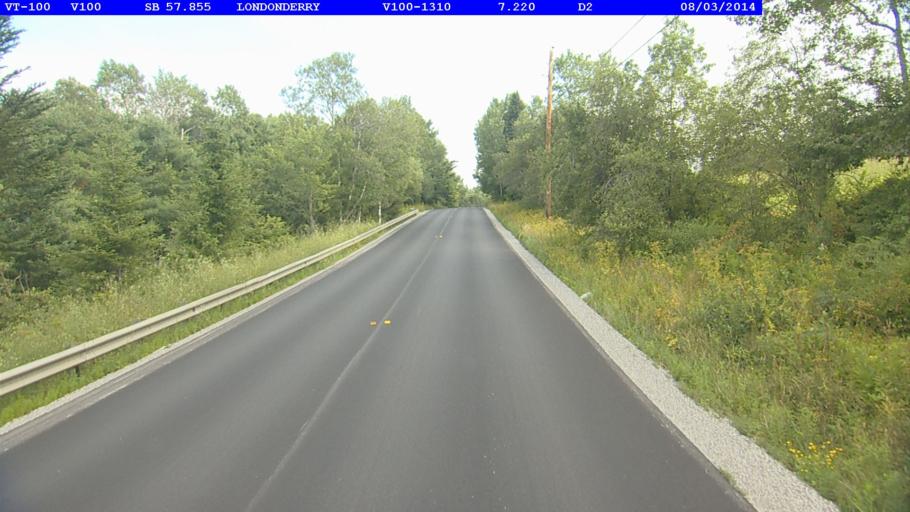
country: US
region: Vermont
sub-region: Windsor County
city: Chester
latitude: 43.2437
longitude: -72.7959
